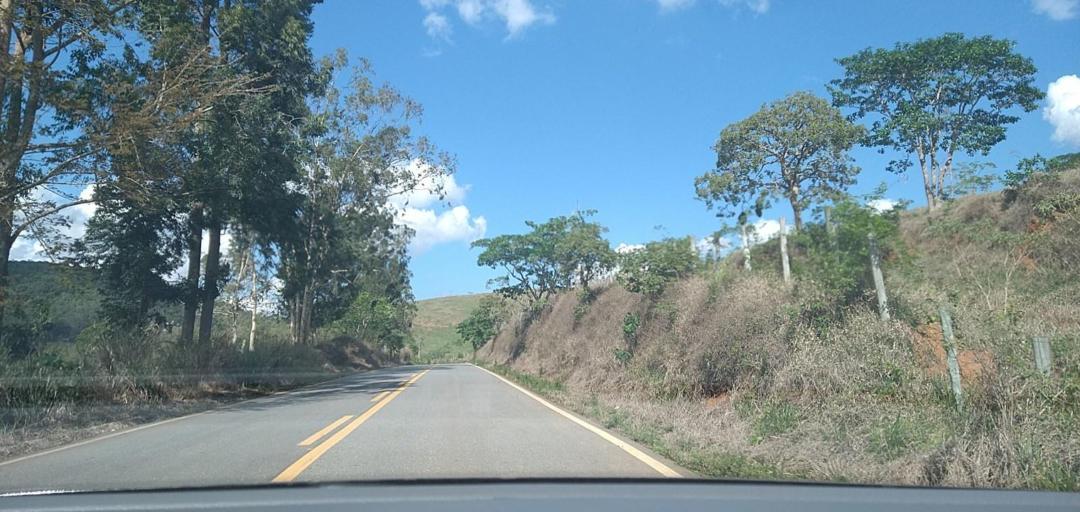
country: BR
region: Minas Gerais
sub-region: Alvinopolis
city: Alvinopolis
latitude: -20.0166
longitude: -43.0900
